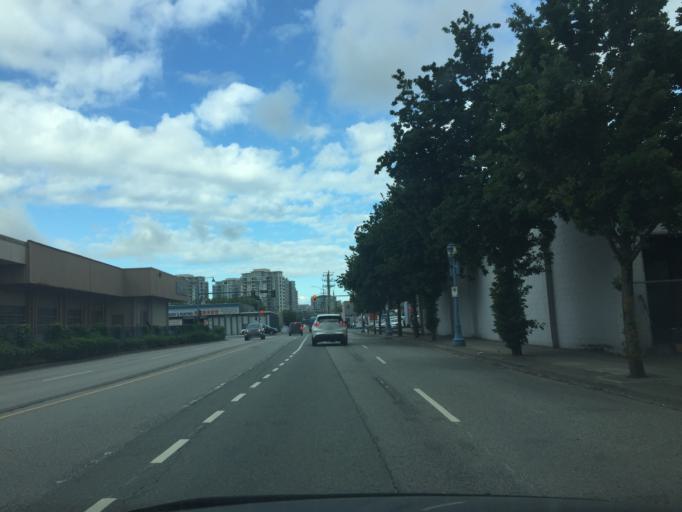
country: CA
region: British Columbia
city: Richmond
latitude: 49.1739
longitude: -123.1387
